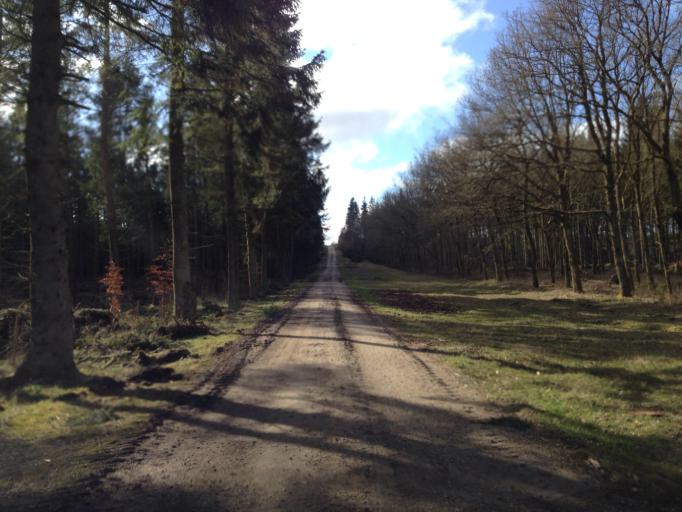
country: DK
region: Central Jutland
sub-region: Holstebro Kommune
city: Ulfborg
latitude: 56.2675
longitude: 8.4630
